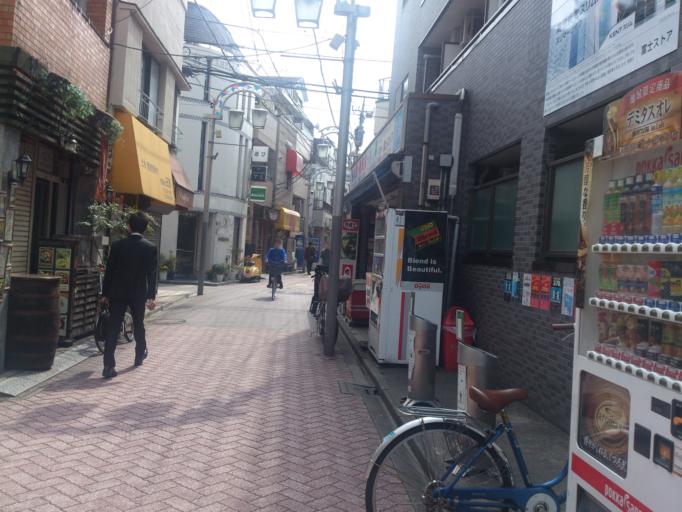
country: JP
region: Tokyo
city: Tokyo
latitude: 35.7088
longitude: 139.6517
